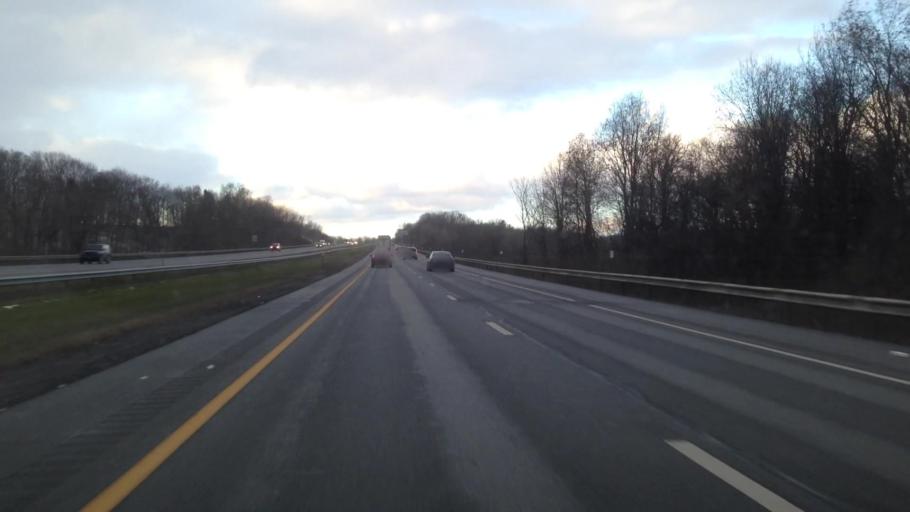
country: US
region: New York
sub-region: Herkimer County
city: Little Falls
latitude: 43.0104
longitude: -74.7900
